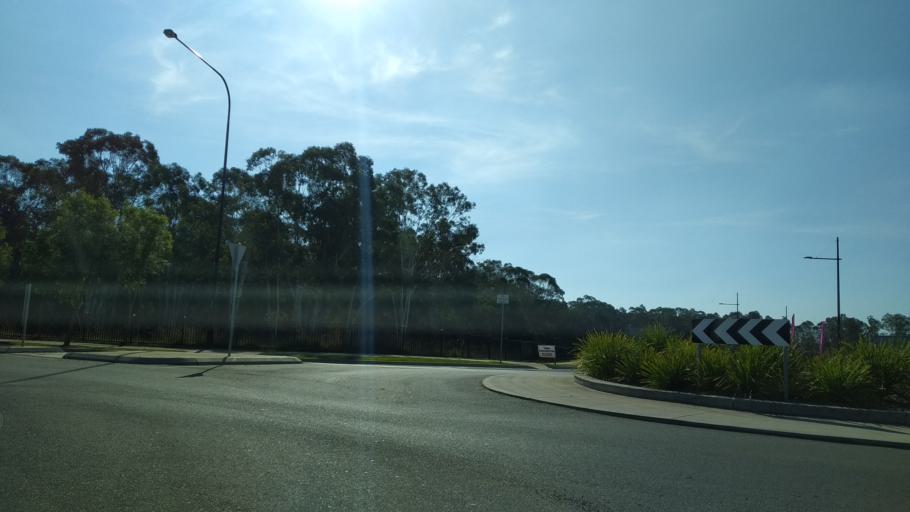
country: AU
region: New South Wales
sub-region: Blacktown
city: Hassall Grove
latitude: -33.7233
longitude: 150.8490
